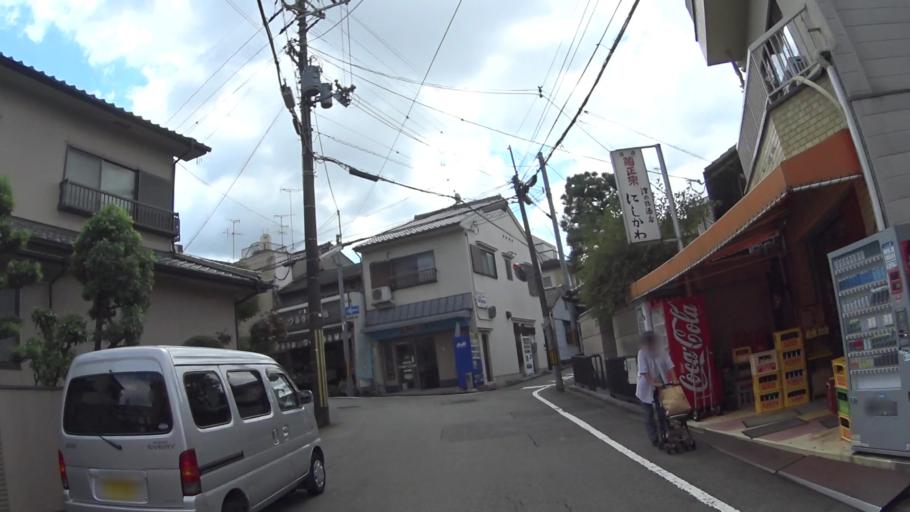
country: JP
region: Kyoto
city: Kyoto
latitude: 34.9851
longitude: 135.7751
